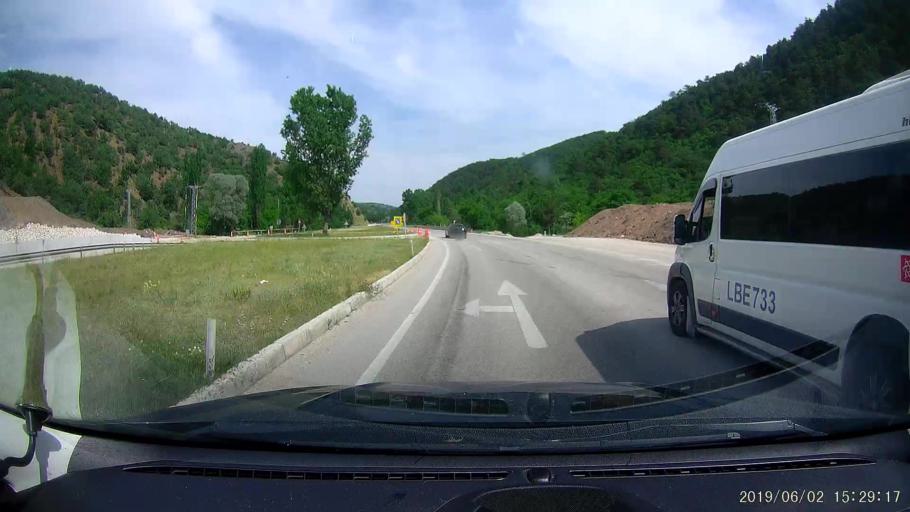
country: TR
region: Amasya
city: Saraycik
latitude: 40.9687
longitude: 35.0854
